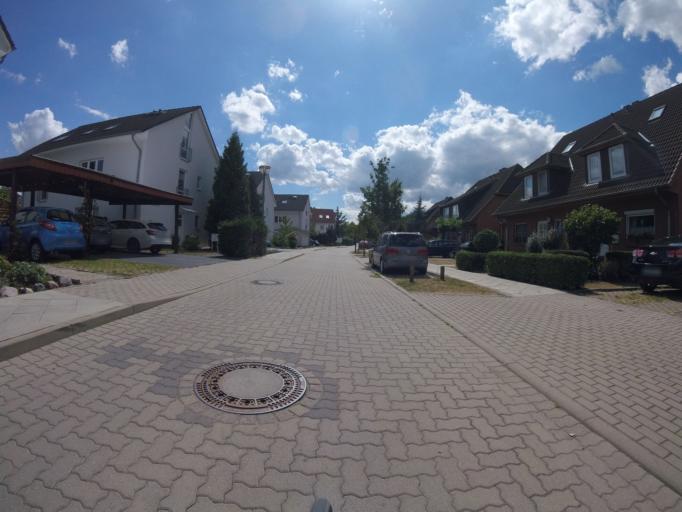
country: DE
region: Brandenburg
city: Werder
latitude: 52.4119
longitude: 12.9880
